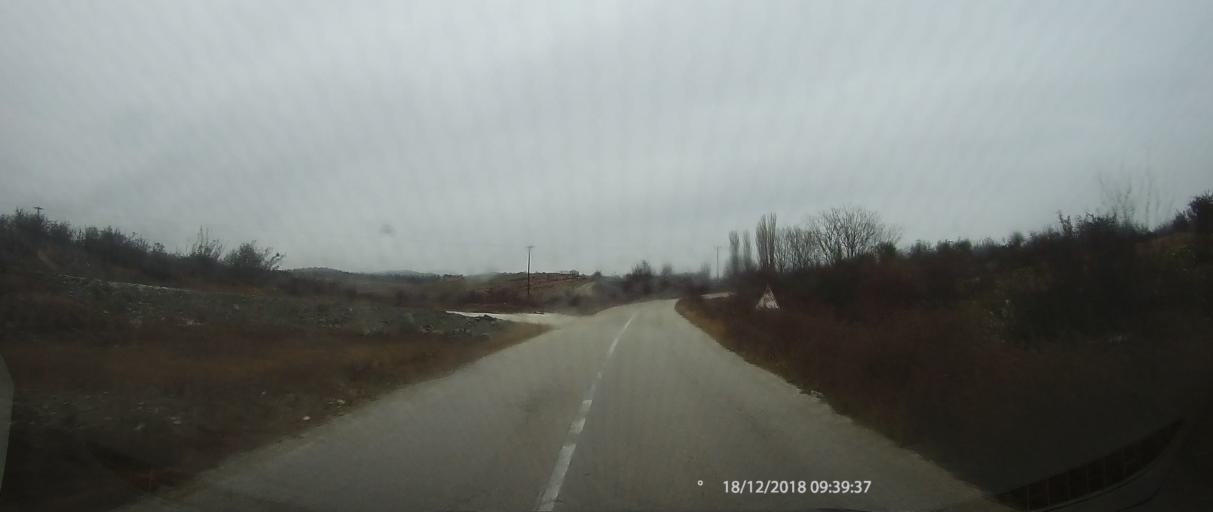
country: GR
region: Thessaly
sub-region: Nomos Larisis
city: Elassona
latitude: 40.0006
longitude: 22.2179
